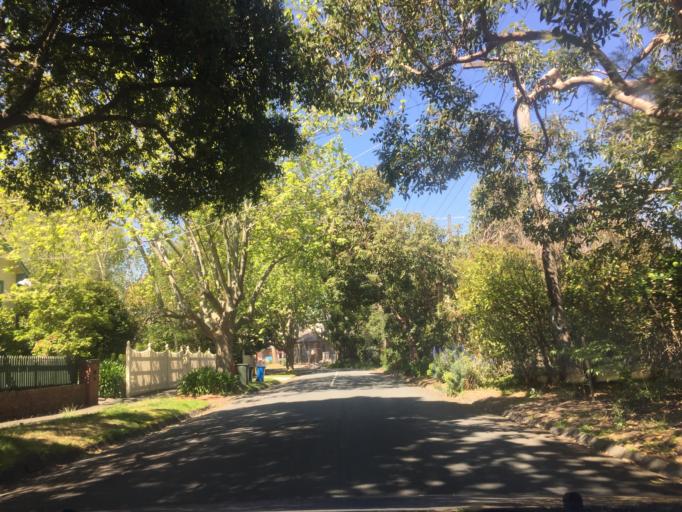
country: AU
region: Victoria
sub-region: Boroondara
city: Canterbury
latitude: -37.8255
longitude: 145.0744
